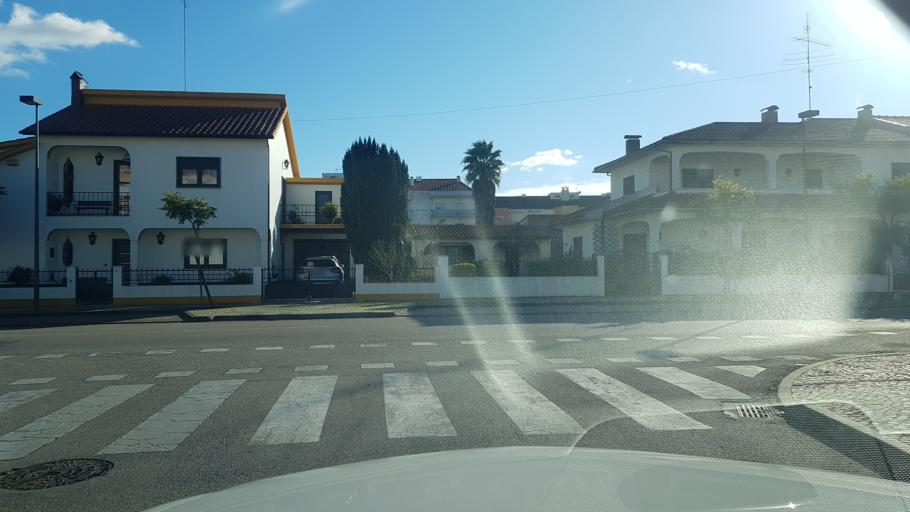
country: PT
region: Santarem
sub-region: Entroncamento
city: Entroncamento
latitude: 39.4739
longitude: -8.4747
